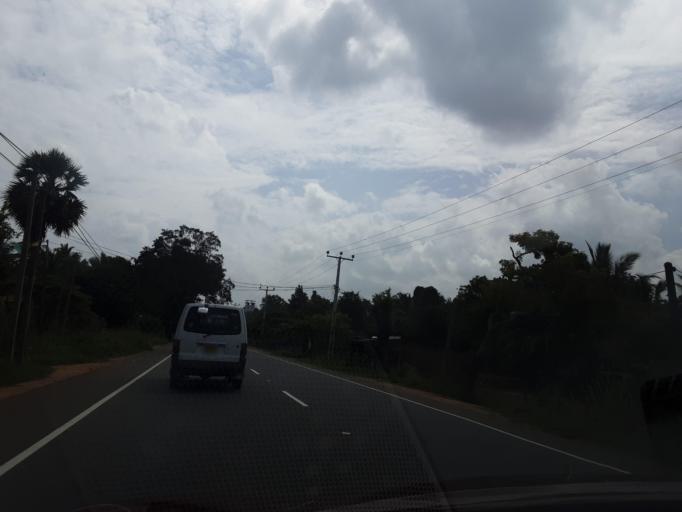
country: LK
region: North Central
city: Anuradhapura
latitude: 8.4731
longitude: 80.5127
